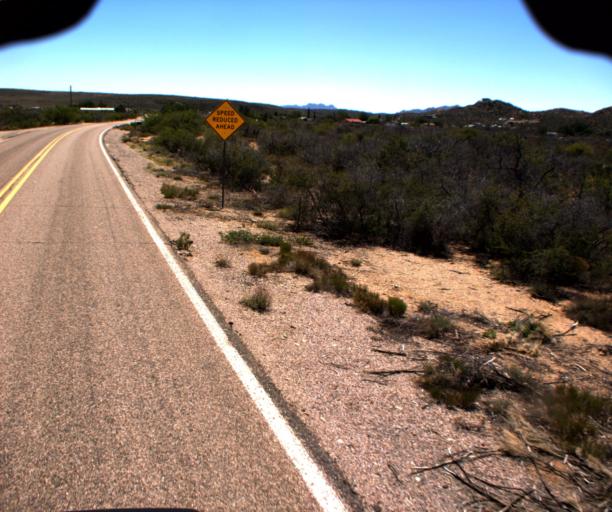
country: US
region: Arizona
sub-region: Yavapai County
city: Congress
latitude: 34.4263
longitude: -112.9162
